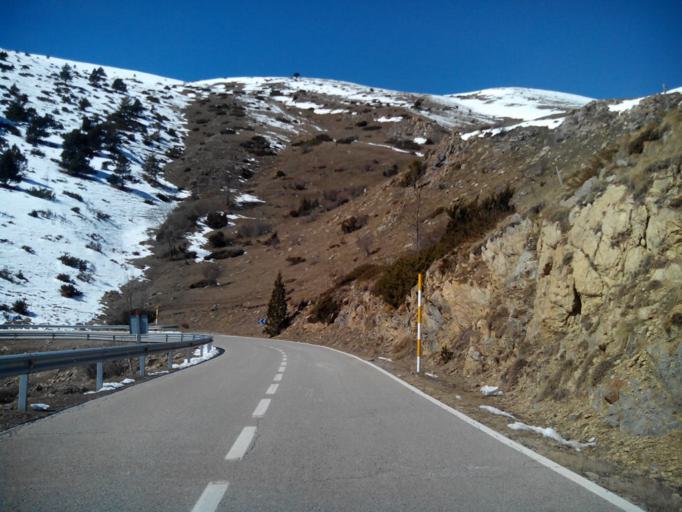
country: ES
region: Catalonia
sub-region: Provincia de Girona
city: Toses
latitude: 42.3137
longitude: 1.9713
